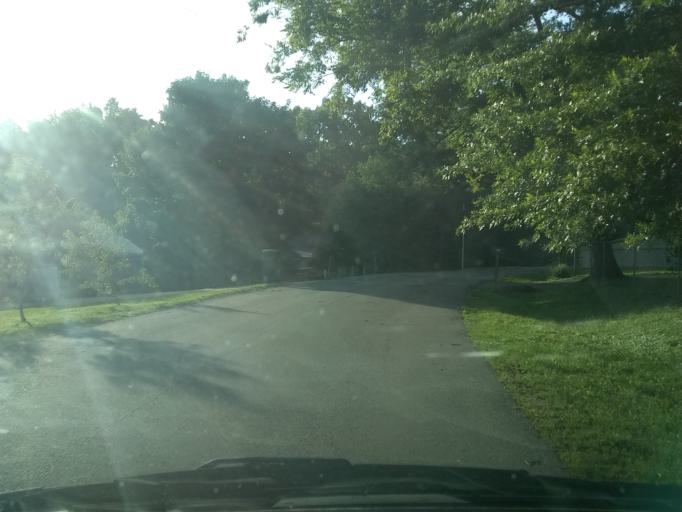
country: US
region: Tennessee
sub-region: Davidson County
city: Nashville
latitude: 36.1308
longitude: -86.7032
